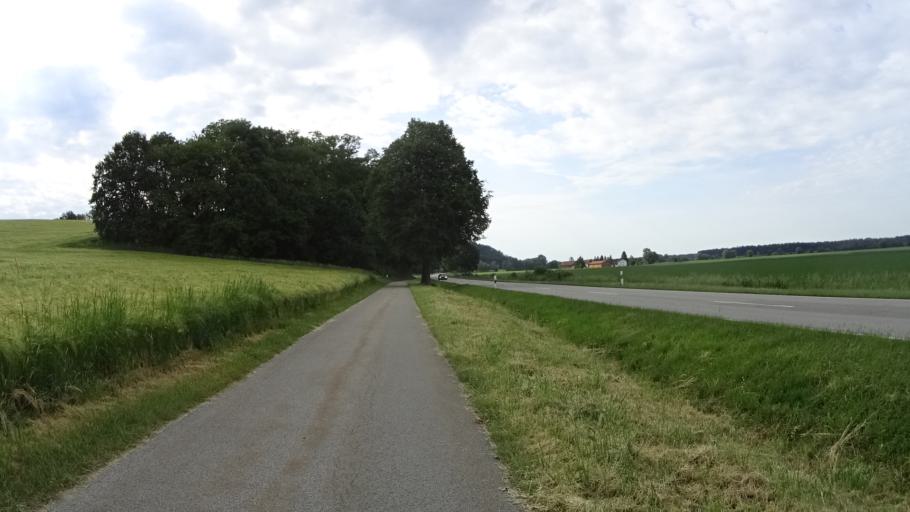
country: DE
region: Bavaria
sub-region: Lower Bavaria
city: Bogen
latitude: 48.8963
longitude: 12.7260
